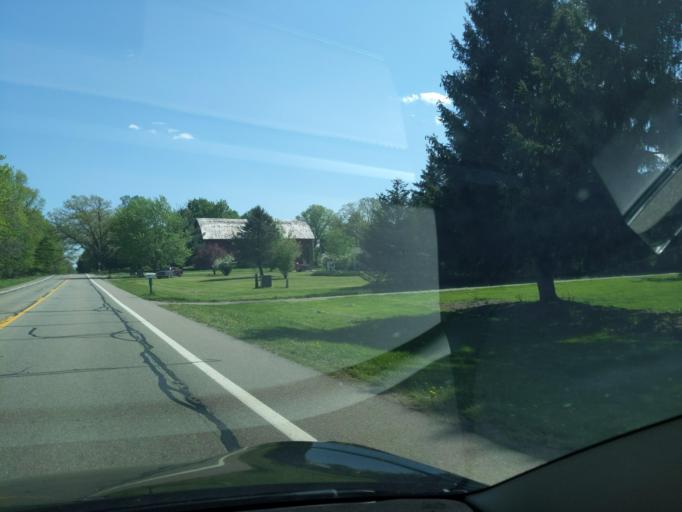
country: US
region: Michigan
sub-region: Kent County
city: Lowell
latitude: 42.8395
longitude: -85.3702
